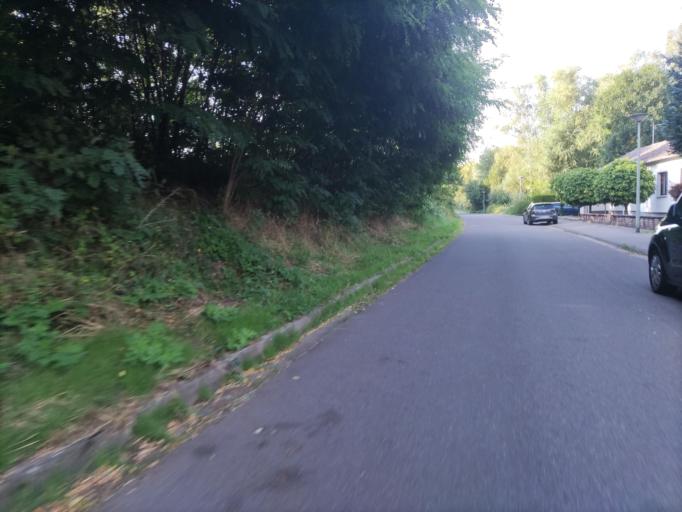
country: DE
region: Saarland
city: Wadgassen
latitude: 49.2641
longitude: 6.8007
